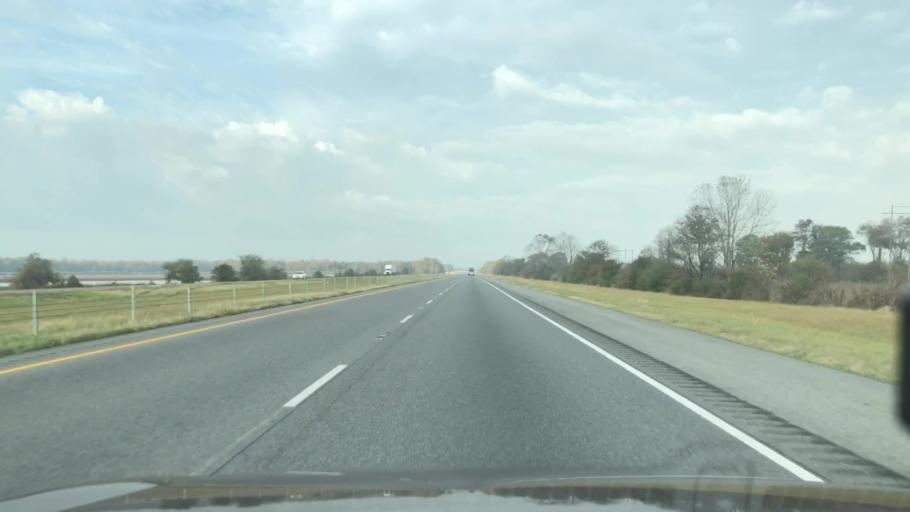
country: US
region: Louisiana
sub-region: Richland Parish
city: Delhi
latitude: 32.4226
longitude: -91.3418
